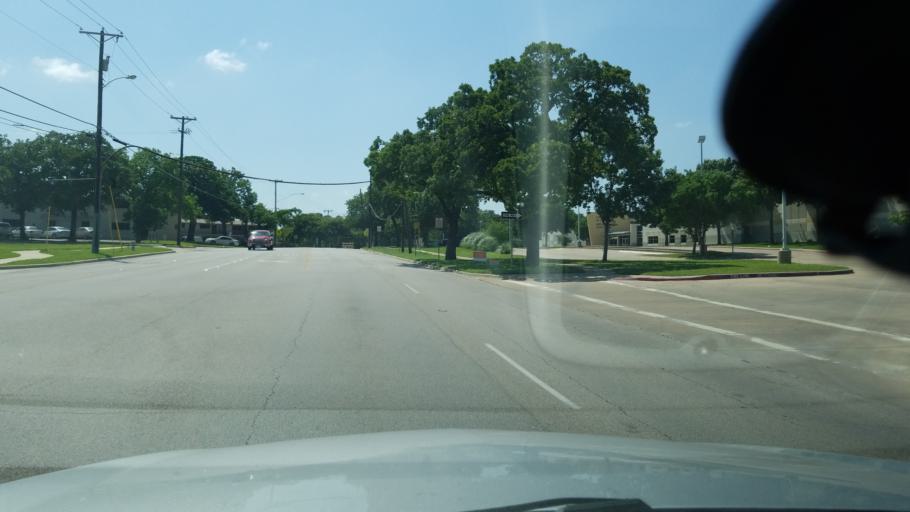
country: US
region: Texas
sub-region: Dallas County
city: Irving
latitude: 32.8186
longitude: -96.9534
